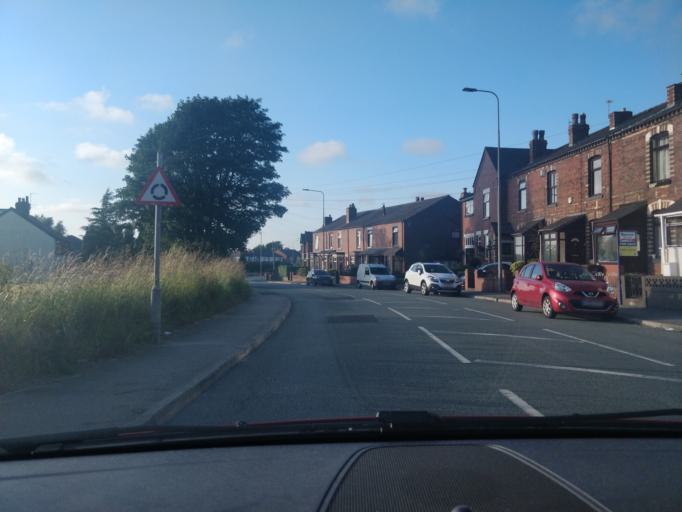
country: GB
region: England
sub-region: St. Helens
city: Billinge
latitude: 53.5248
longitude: -2.7159
